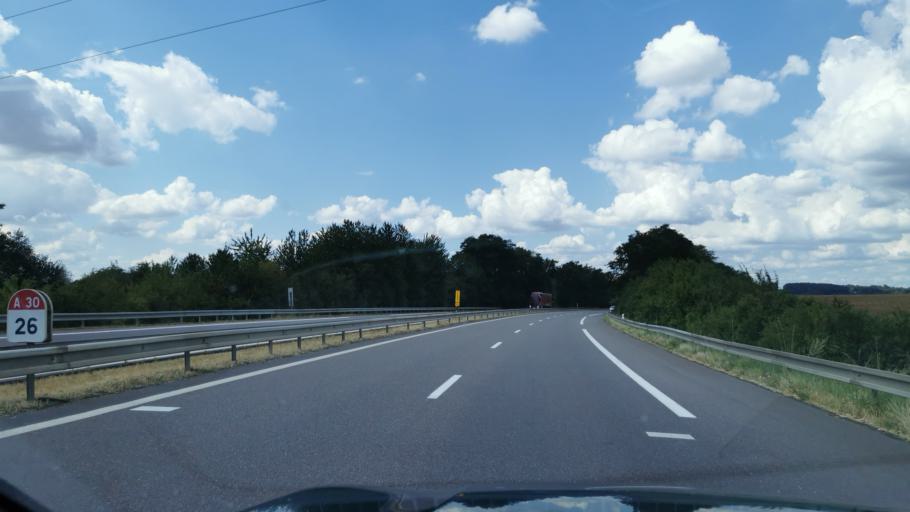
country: FR
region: Lorraine
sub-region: Departement de Meurthe-et-Moselle
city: Crusnes
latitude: 49.4116
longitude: 5.9199
